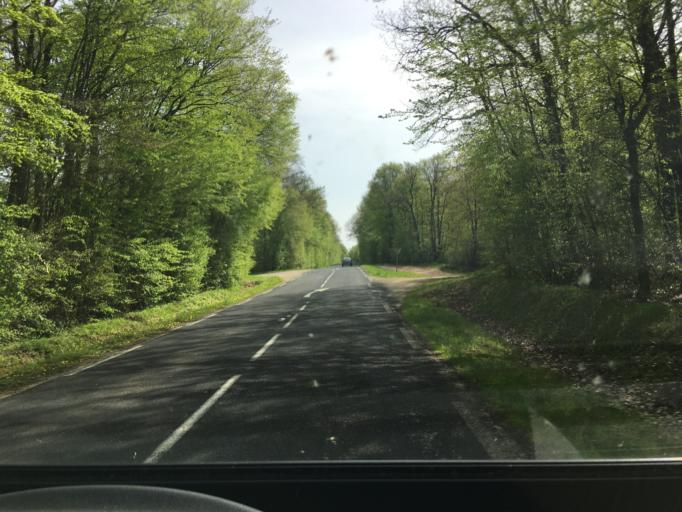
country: FR
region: Lorraine
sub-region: Departement de Meurthe-et-Moselle
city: Velaine-en-Haye
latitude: 48.6641
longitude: 6.0057
